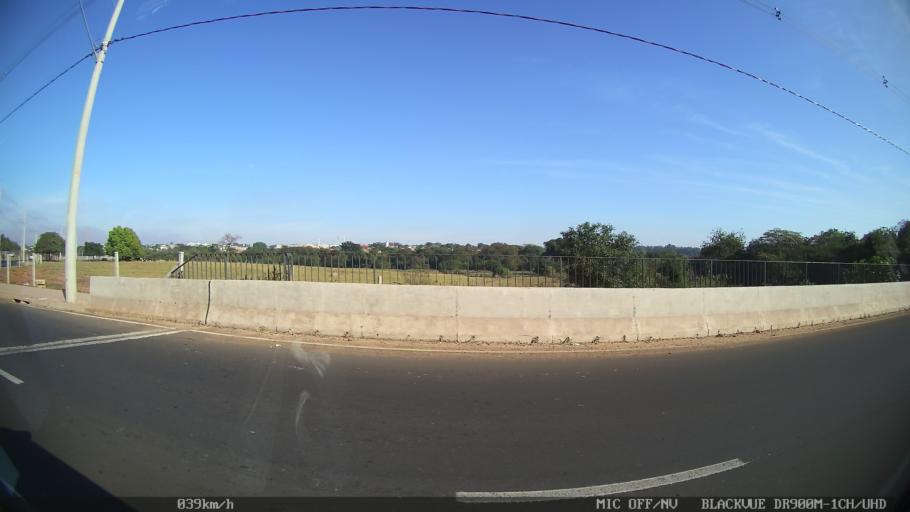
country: BR
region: Sao Paulo
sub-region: Sao Jose Do Rio Preto
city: Sao Jose do Rio Preto
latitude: -20.7596
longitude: -49.3709
